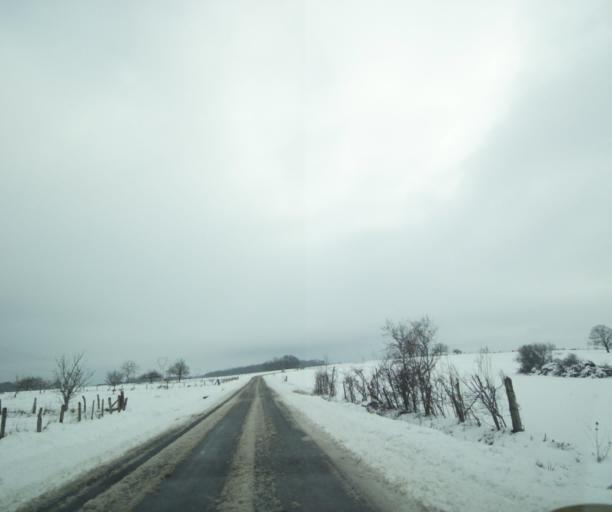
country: FR
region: Champagne-Ardenne
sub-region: Departement de la Haute-Marne
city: Montier-en-Der
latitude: 48.5074
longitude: 4.7286
